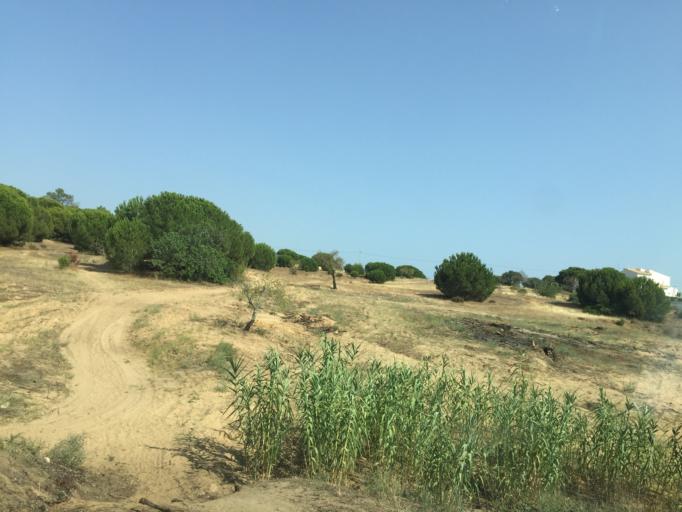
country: PT
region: Faro
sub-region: Albufeira
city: Ferreiras
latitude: 37.0969
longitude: -8.1999
